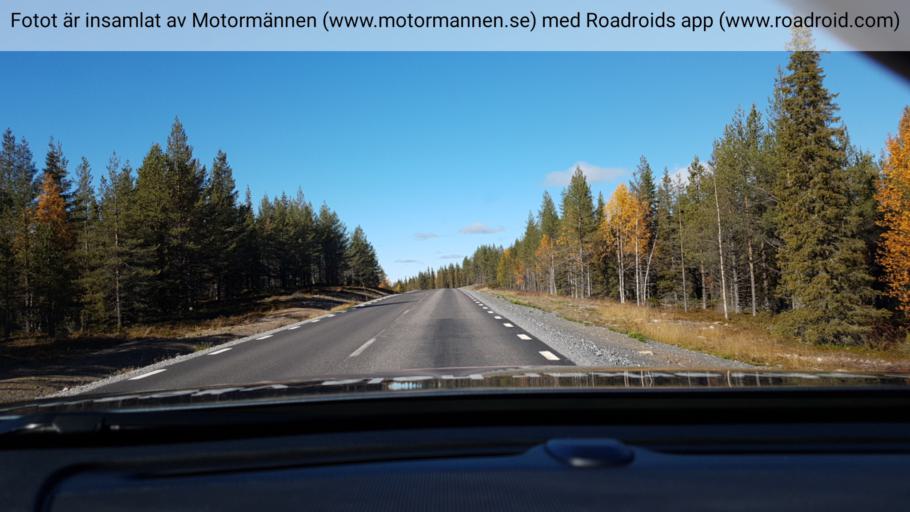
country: SE
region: Norrbotten
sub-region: Gallivare Kommun
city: Gaellivare
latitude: 66.8927
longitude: 20.9223
